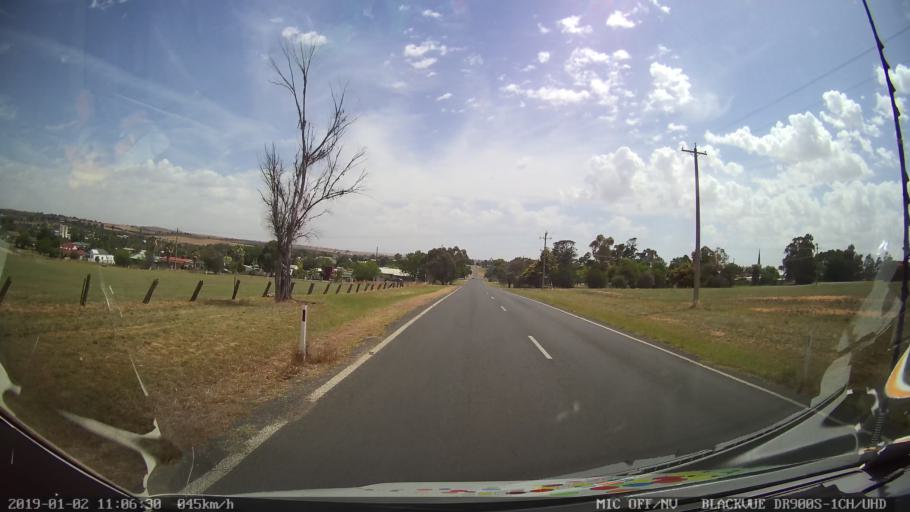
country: AU
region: New South Wales
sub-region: Young
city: Young
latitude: -34.5548
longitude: 148.3567
